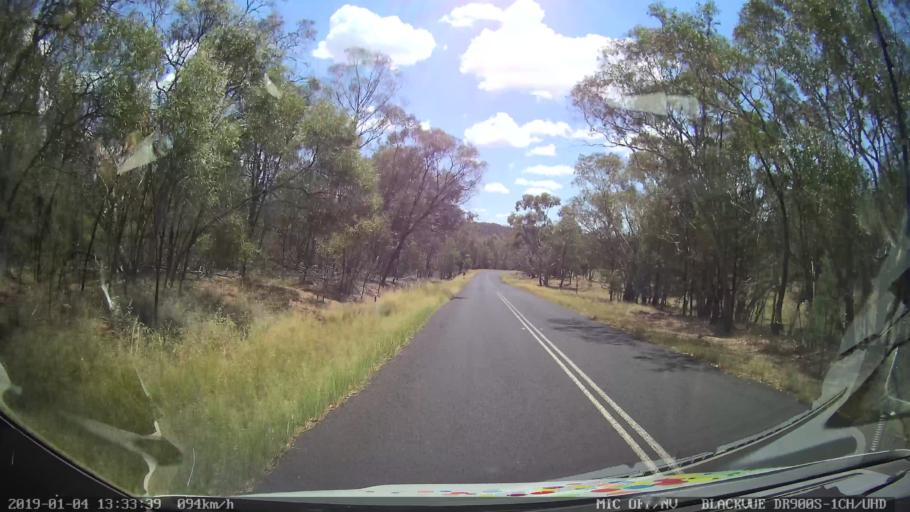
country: AU
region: New South Wales
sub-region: Dubbo Municipality
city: Dubbo
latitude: -32.5953
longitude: 148.5401
